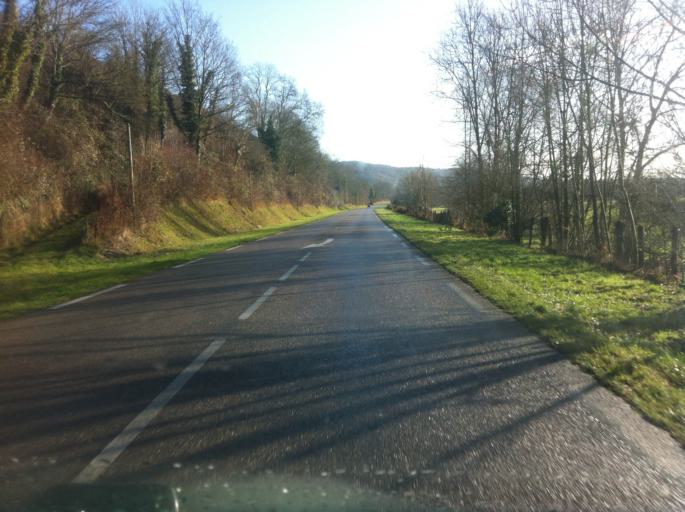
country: FR
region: Haute-Normandie
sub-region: Departement de la Seine-Maritime
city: Saint-Pierre-de-Varengeville
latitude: 49.4828
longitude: 0.9290
